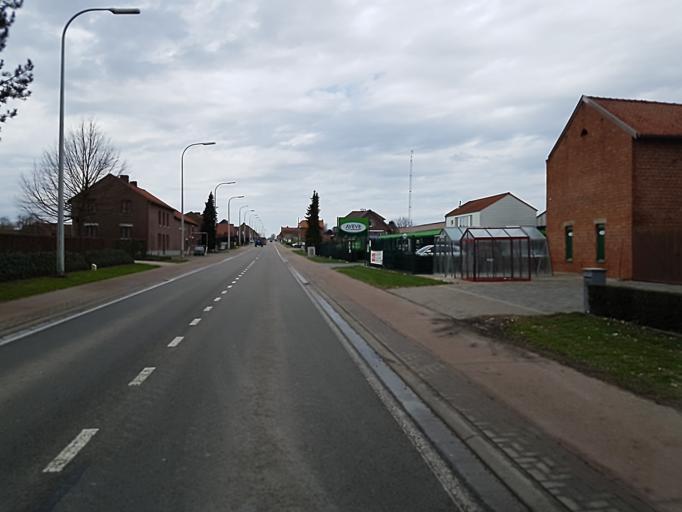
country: BE
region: Flanders
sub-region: Provincie Limburg
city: Borgloon
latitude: 50.7859
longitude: 5.4019
